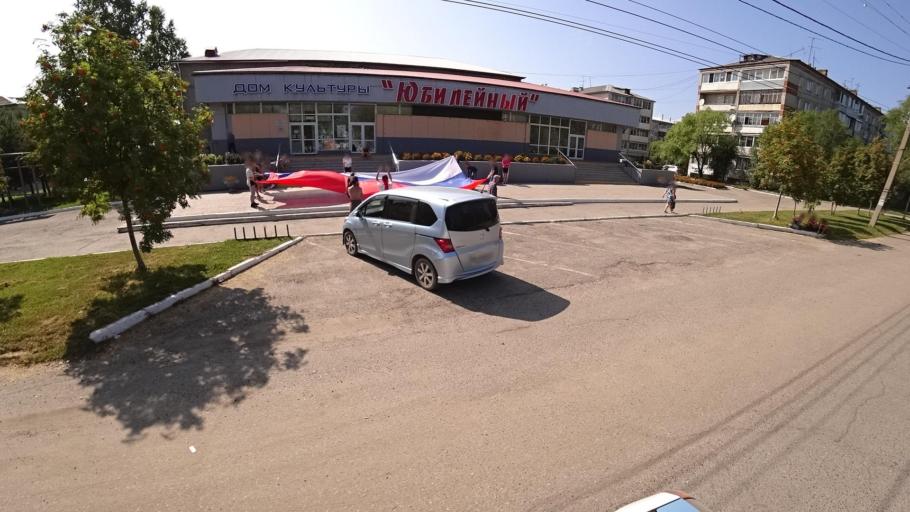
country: RU
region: Khabarovsk Krai
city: Khor
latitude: 47.9672
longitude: 135.0525
